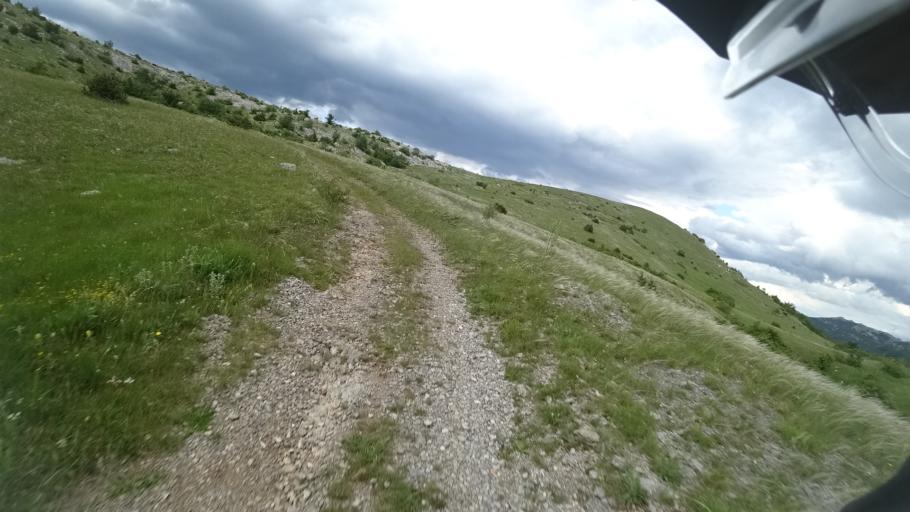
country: HR
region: Zadarska
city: Obrovac
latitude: 44.2668
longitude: 15.7256
